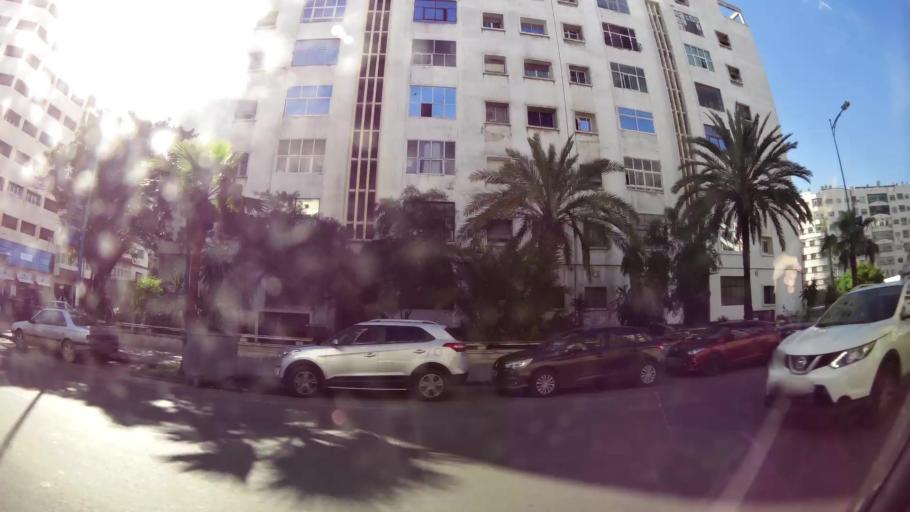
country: MA
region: Grand Casablanca
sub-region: Casablanca
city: Casablanca
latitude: 33.5939
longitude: -7.5966
